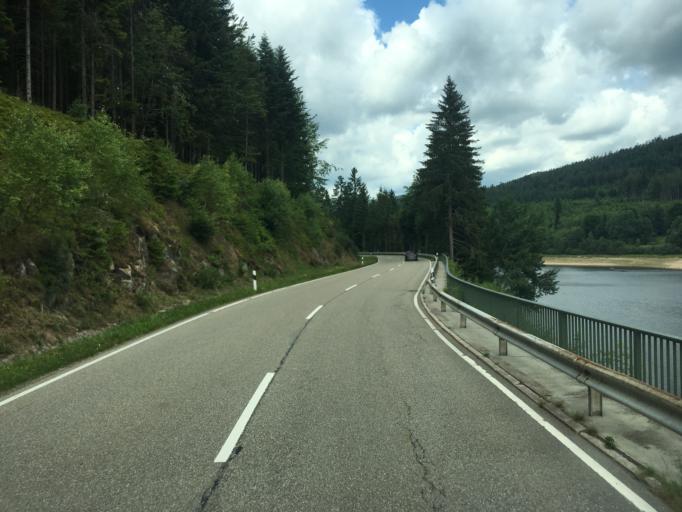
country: DE
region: Baden-Wuerttemberg
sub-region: Karlsruhe Region
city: Forbach
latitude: 48.6585
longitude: 8.3201
